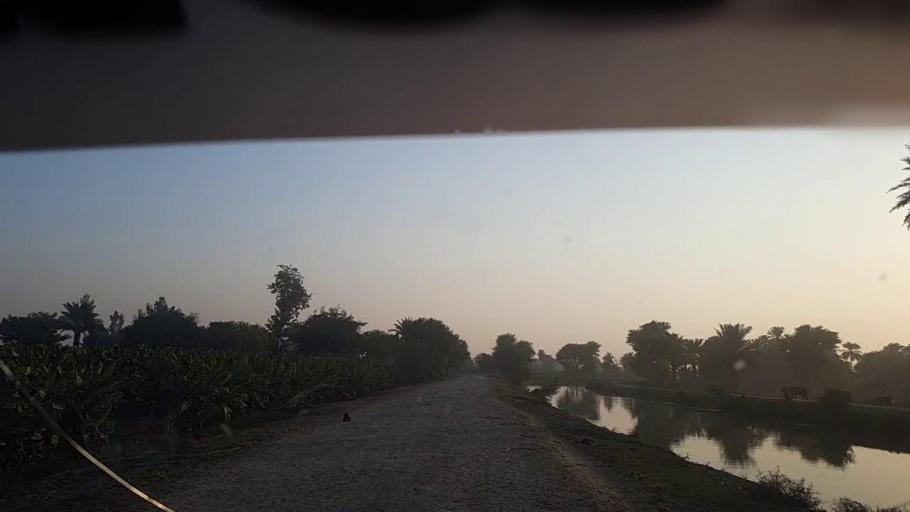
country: PK
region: Sindh
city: Ranipur
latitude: 27.2331
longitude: 68.5486
